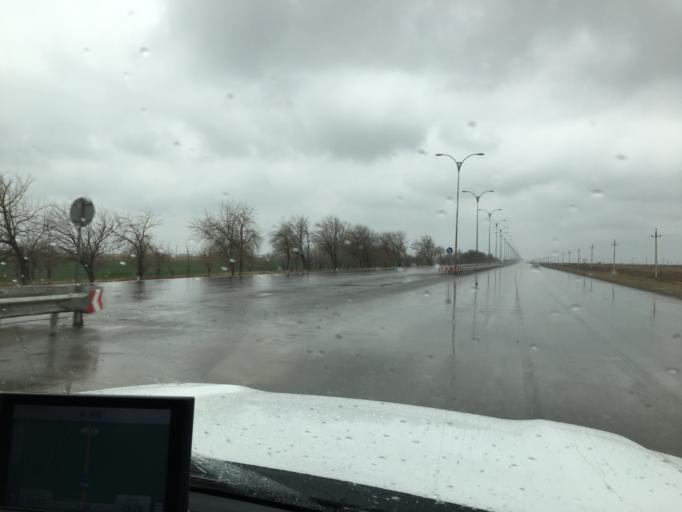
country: TM
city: Murgab
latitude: 37.5071
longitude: 61.9453
